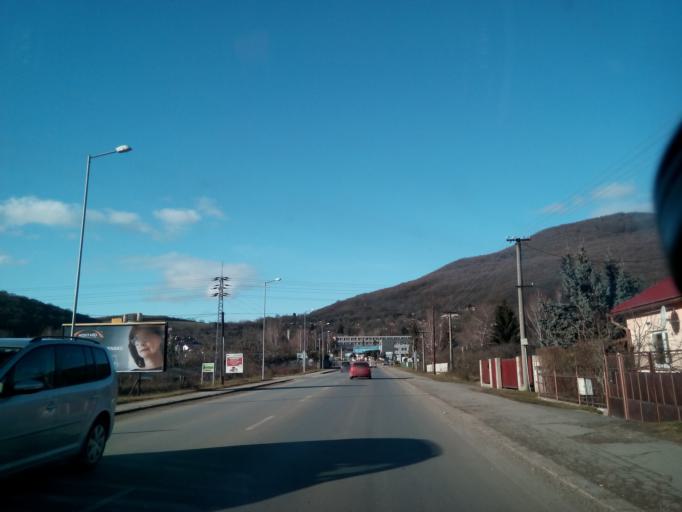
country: SK
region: Kosicky
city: Roznava
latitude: 48.6603
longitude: 20.5180
